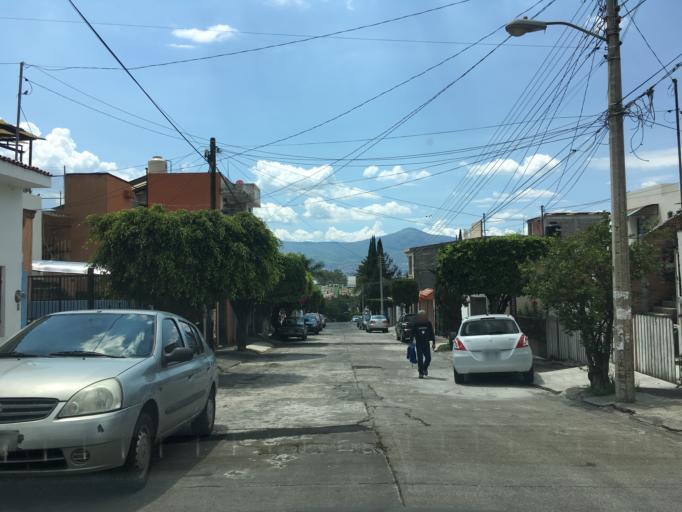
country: MX
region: Michoacan
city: Morelia
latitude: 19.6707
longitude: -101.1995
